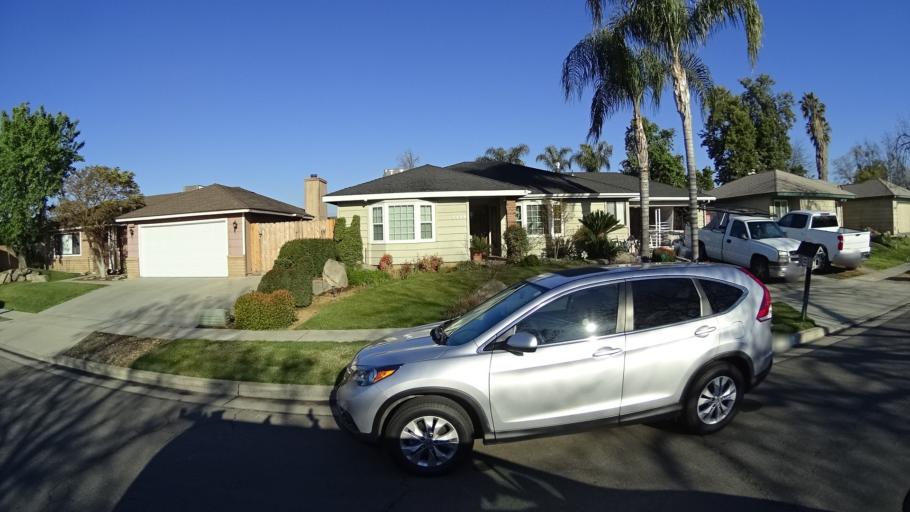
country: US
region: California
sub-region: Fresno County
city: West Park
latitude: 36.8149
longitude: -119.8749
